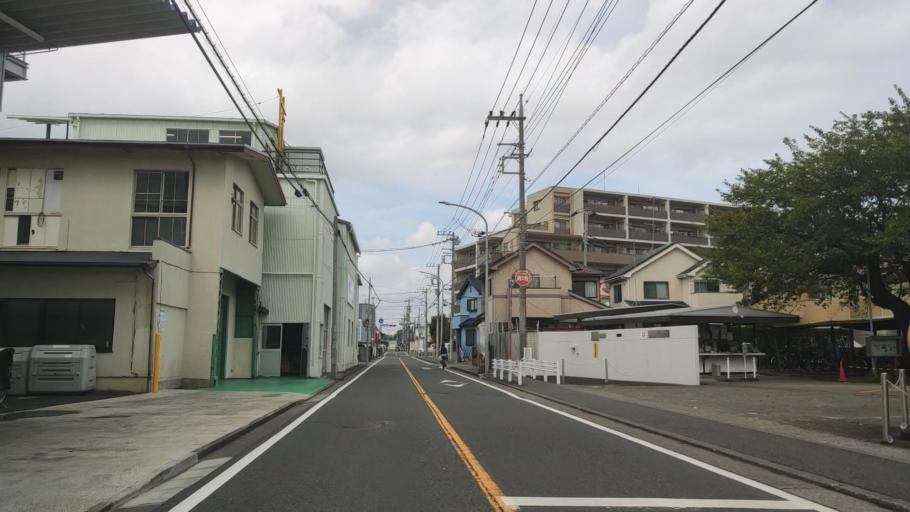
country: JP
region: Kanagawa
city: Minami-rinkan
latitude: 35.4773
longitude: 139.4756
